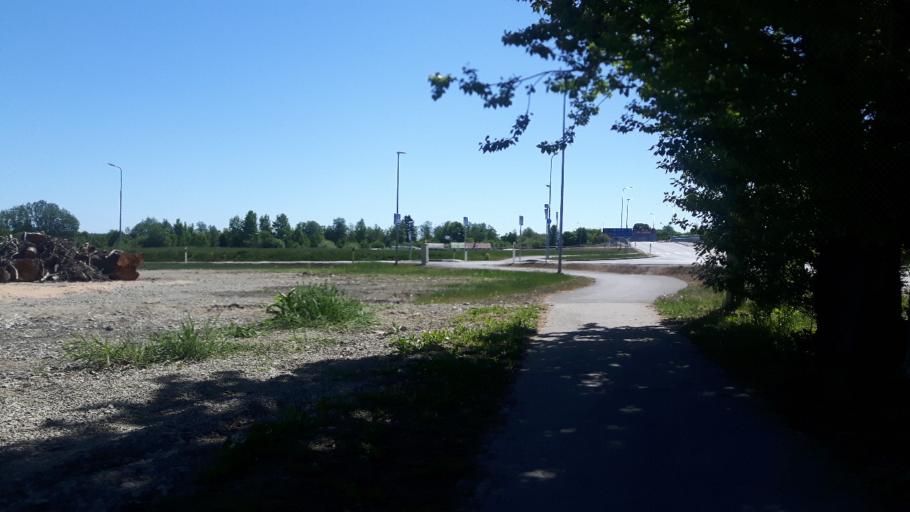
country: EE
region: Ida-Virumaa
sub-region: Sillamaee linn
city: Sillamae
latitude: 59.3923
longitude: 27.7499
